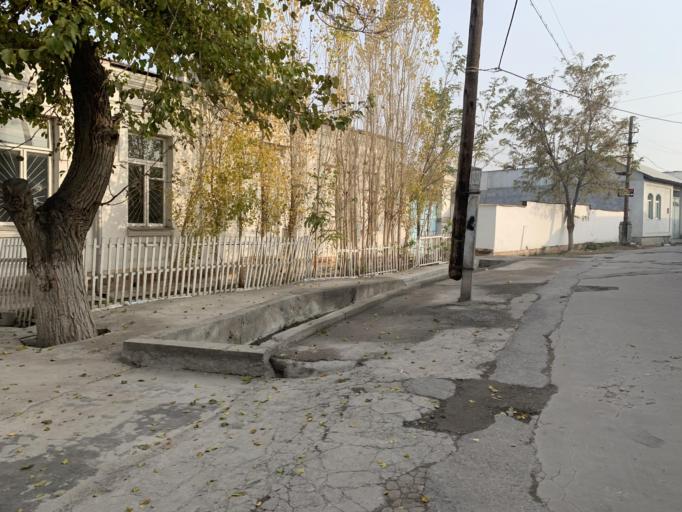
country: UZ
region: Fergana
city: Qo`qon
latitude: 40.5393
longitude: 70.9291
